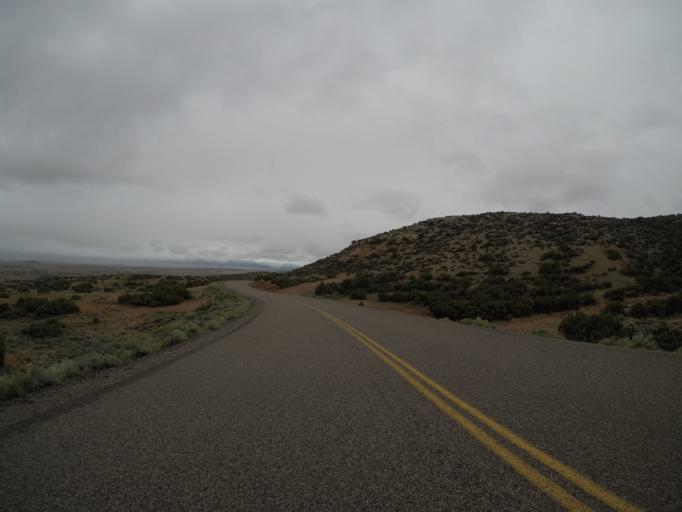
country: US
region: Wyoming
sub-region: Big Horn County
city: Lovell
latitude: 45.0255
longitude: -108.2620
